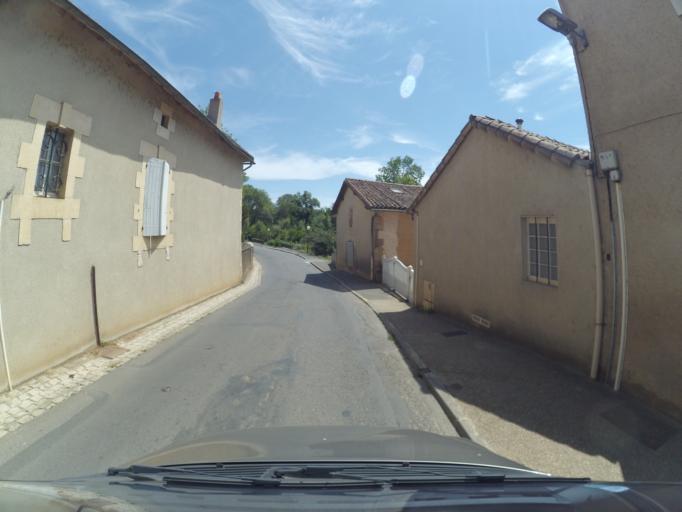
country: FR
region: Poitou-Charentes
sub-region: Departement de la Vienne
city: Vivonne
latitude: 46.4185
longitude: 0.3109
